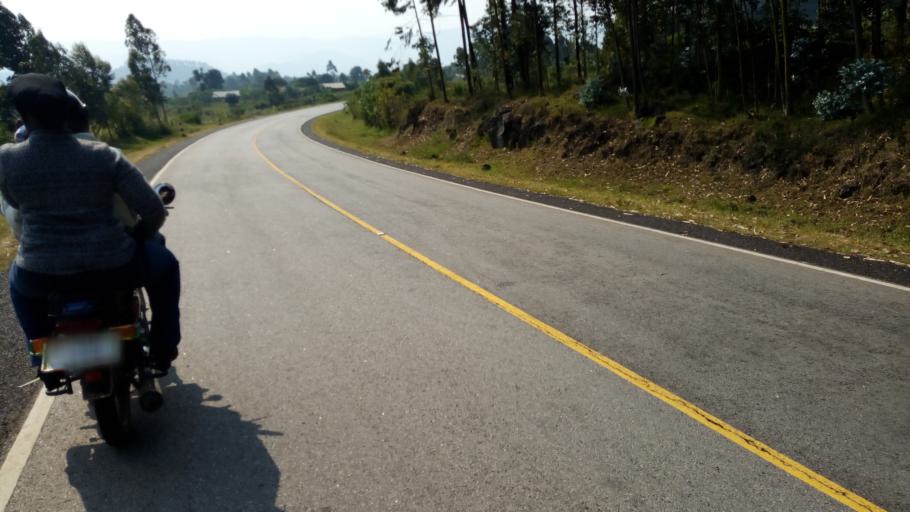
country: UG
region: Western Region
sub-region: Kisoro District
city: Kisoro
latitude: -1.3288
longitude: 29.7317
